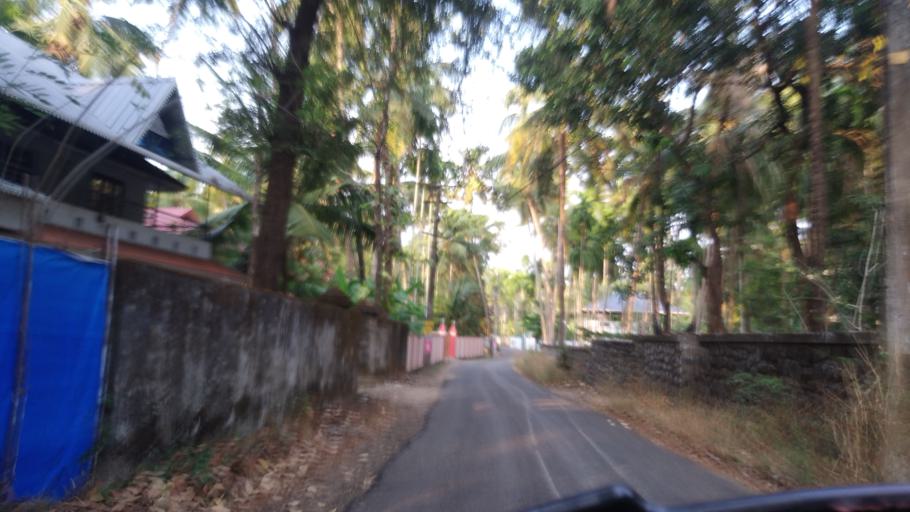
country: IN
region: Kerala
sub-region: Thrissur District
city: Thanniyam
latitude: 10.4090
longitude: 76.0913
